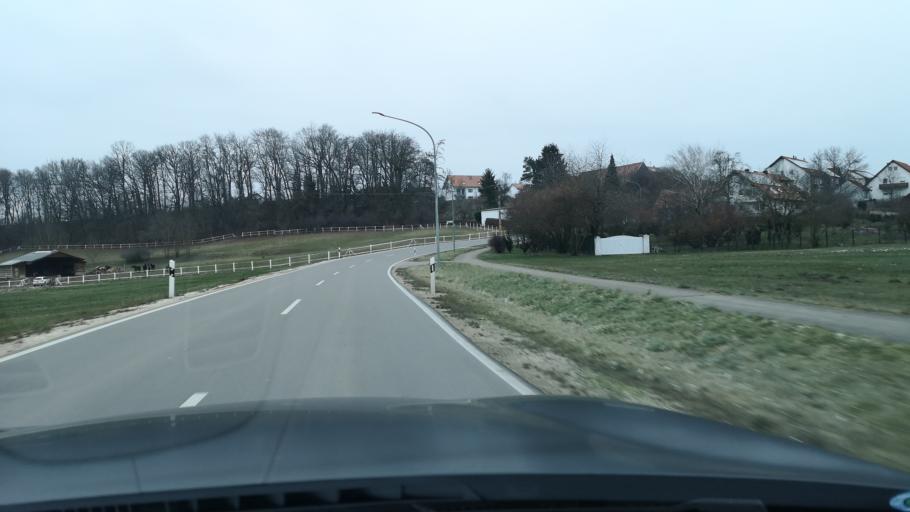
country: DE
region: Bavaria
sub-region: Swabia
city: Leipheim
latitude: 48.4237
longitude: 10.1878
